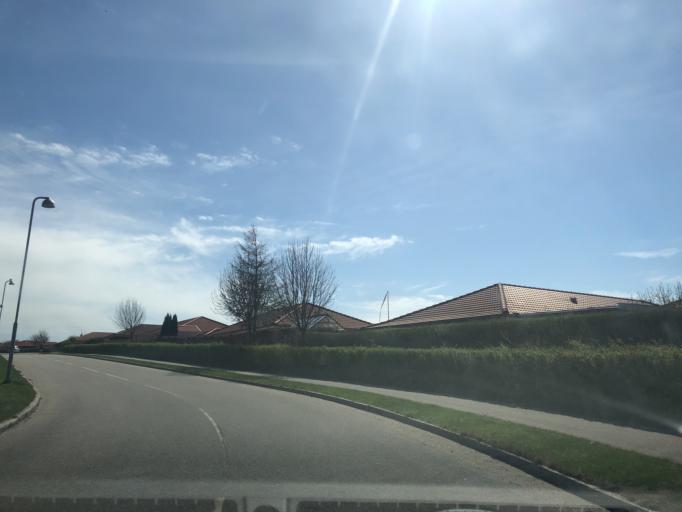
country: DK
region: Zealand
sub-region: Ringsted Kommune
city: Ringsted
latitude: 55.4526
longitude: 11.7791
